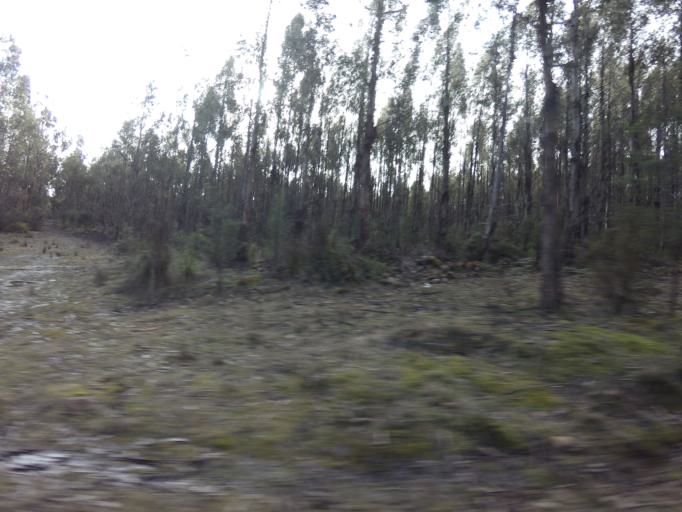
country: AU
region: Tasmania
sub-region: Derwent Valley
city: New Norfolk
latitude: -42.7814
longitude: 146.9063
